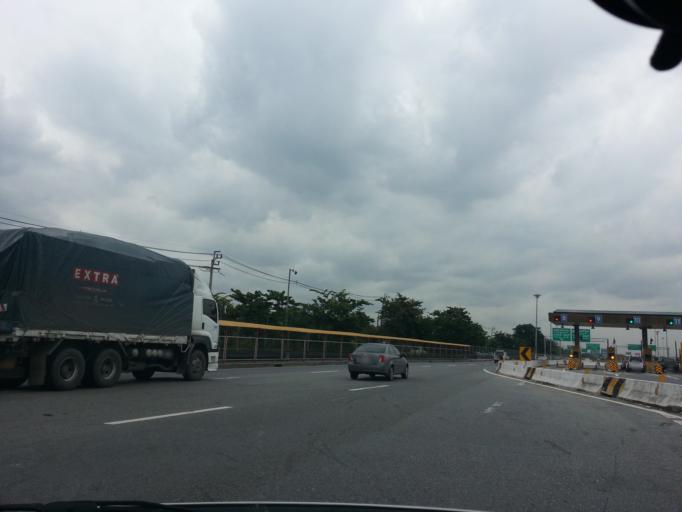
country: TH
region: Bangkok
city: Saphan Sung
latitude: 13.7740
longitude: 100.6890
